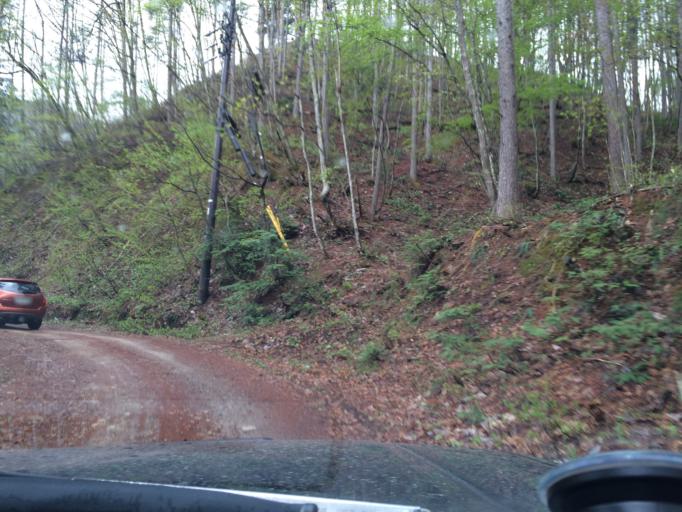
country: JP
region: Nagano
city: Omachi
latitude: 36.5089
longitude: 137.7974
